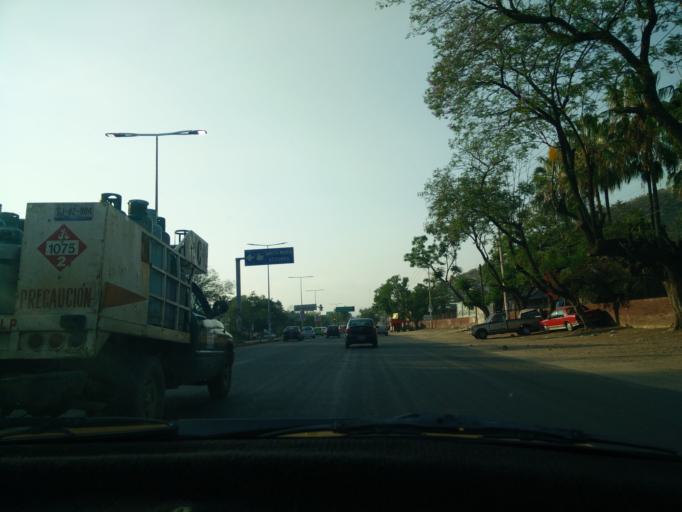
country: MX
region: Oaxaca
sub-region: Santa Maria Atzompa
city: San Jeronimo Yahuiche
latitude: 17.1023
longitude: -96.7520
